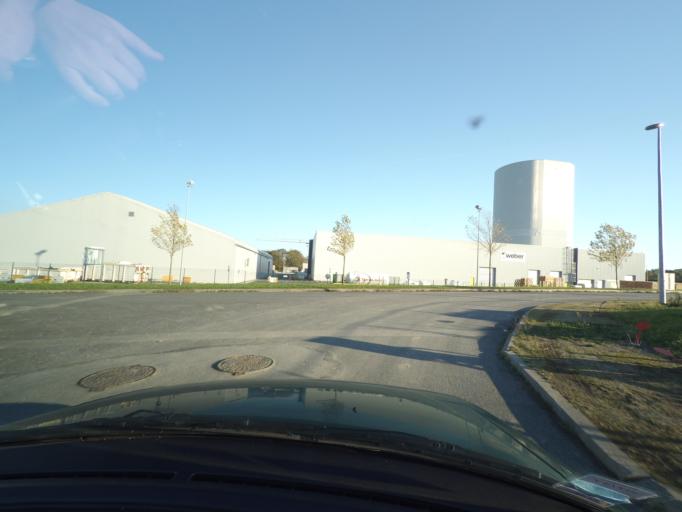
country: FR
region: Pays de la Loire
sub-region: Departement de la Loire-Atlantique
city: Le Bignon
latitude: 47.0992
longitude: -1.4519
